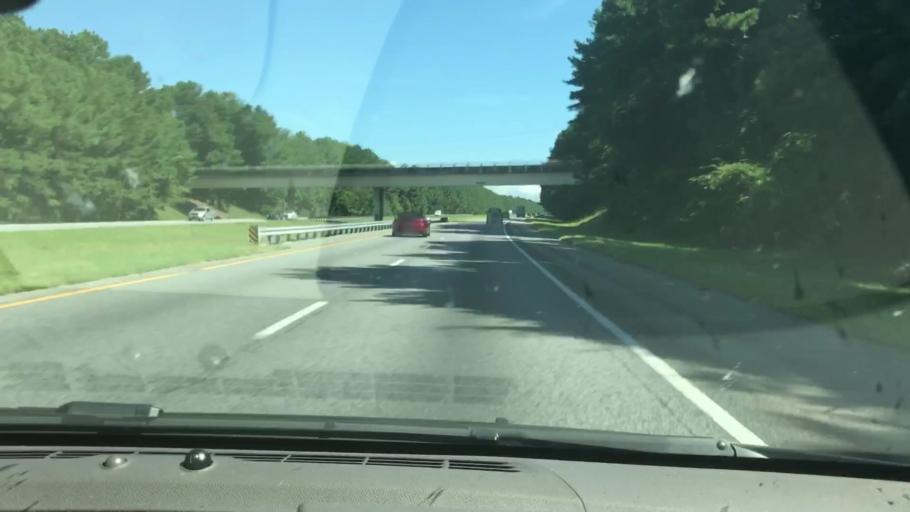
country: US
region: Alabama
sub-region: Russell County
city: Phenix City
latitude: 32.5820
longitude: -84.9608
